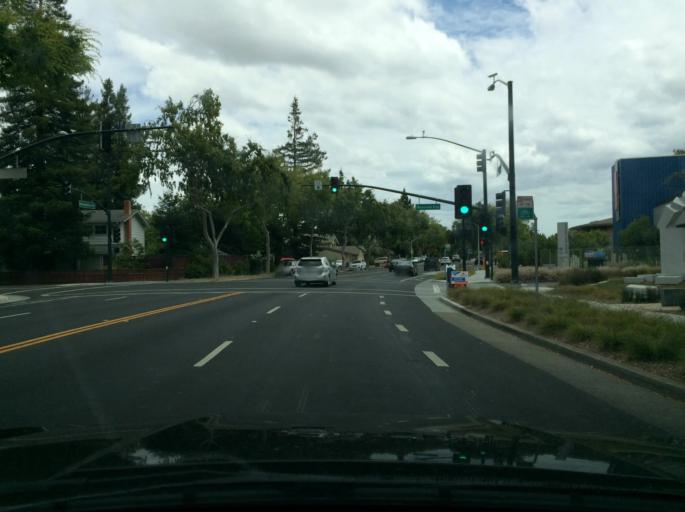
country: US
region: California
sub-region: Santa Clara County
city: Palo Alto
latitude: 37.4229
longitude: -122.1128
